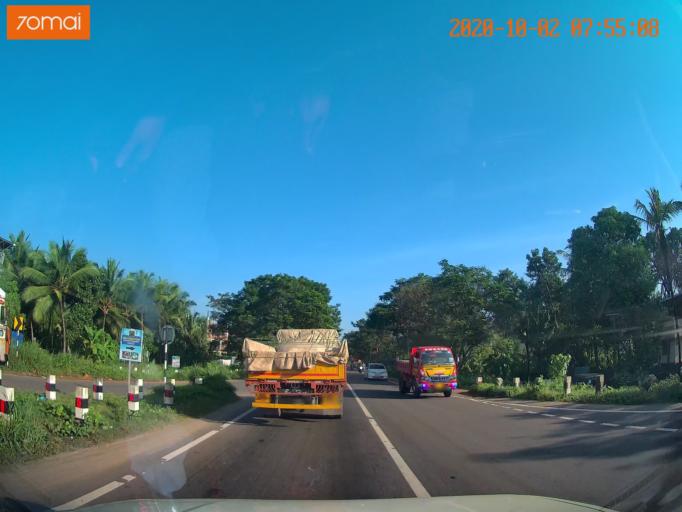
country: IN
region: Kerala
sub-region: Kozhikode
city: Ferokh
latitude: 11.1804
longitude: 75.8723
